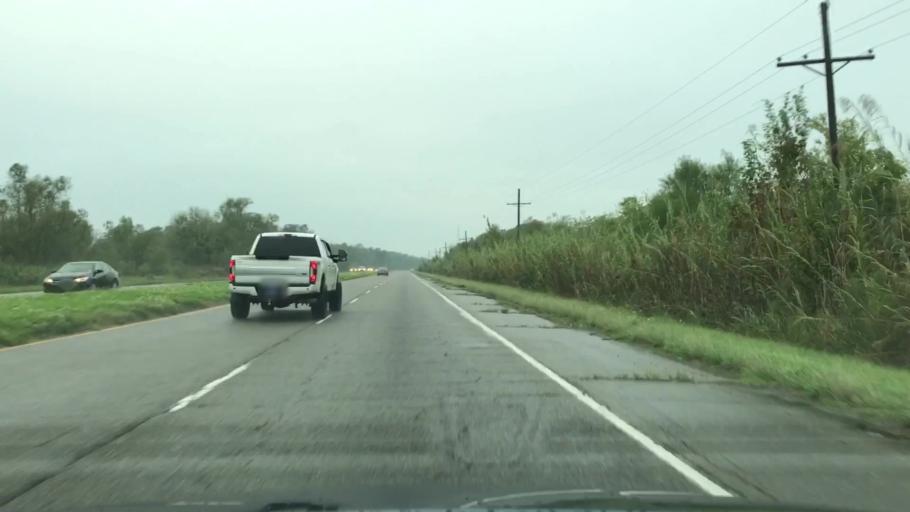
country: US
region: Louisiana
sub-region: Saint Charles Parish
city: Des Allemands
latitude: 29.7938
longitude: -90.5103
